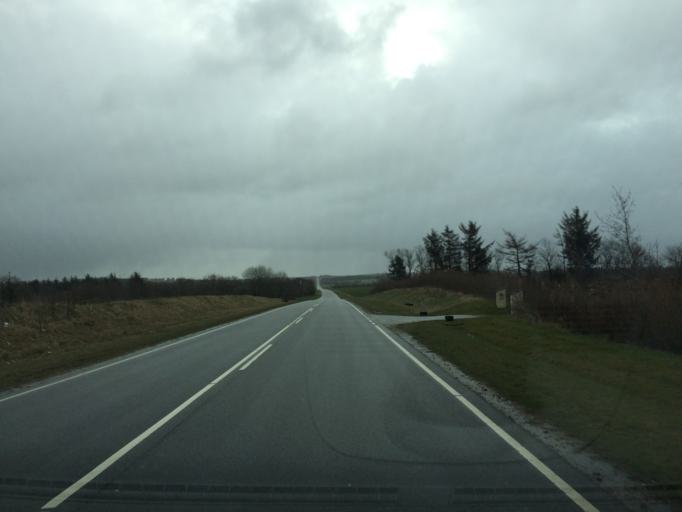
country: DK
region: Central Jutland
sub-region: Ringkobing-Skjern Kommune
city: Videbaek
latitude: 56.1917
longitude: 8.5809
